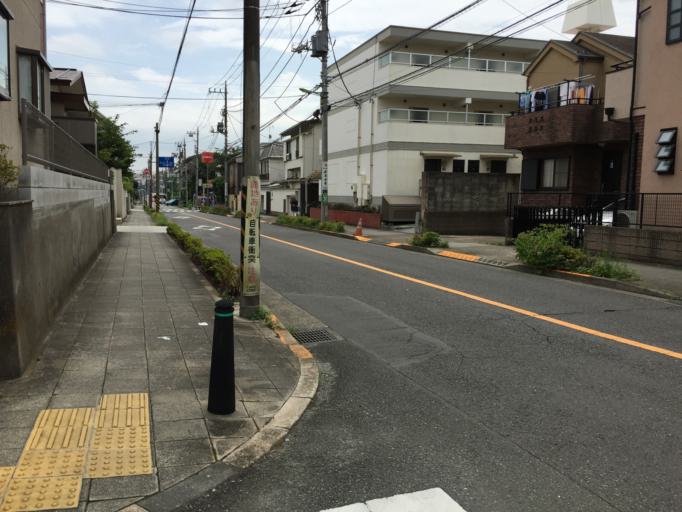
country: JP
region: Tokyo
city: Tokyo
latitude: 35.6581
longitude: 139.6379
